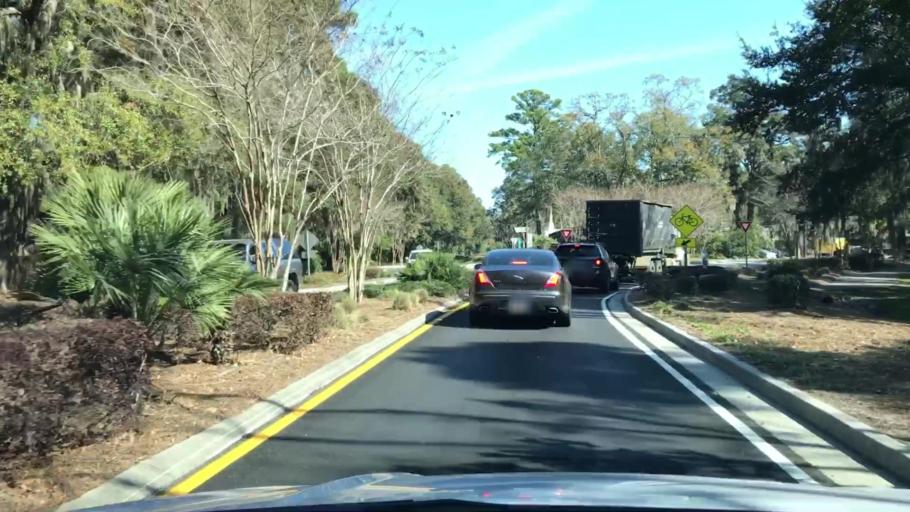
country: US
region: South Carolina
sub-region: Beaufort County
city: Hilton Head Island
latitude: 32.2226
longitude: -80.7086
